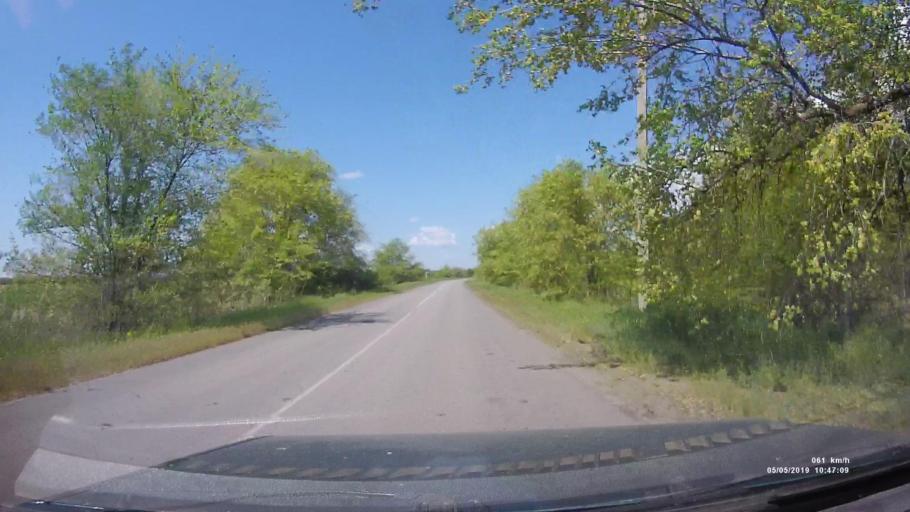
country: RU
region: Rostov
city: Ust'-Donetskiy
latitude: 47.6375
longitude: 40.8369
